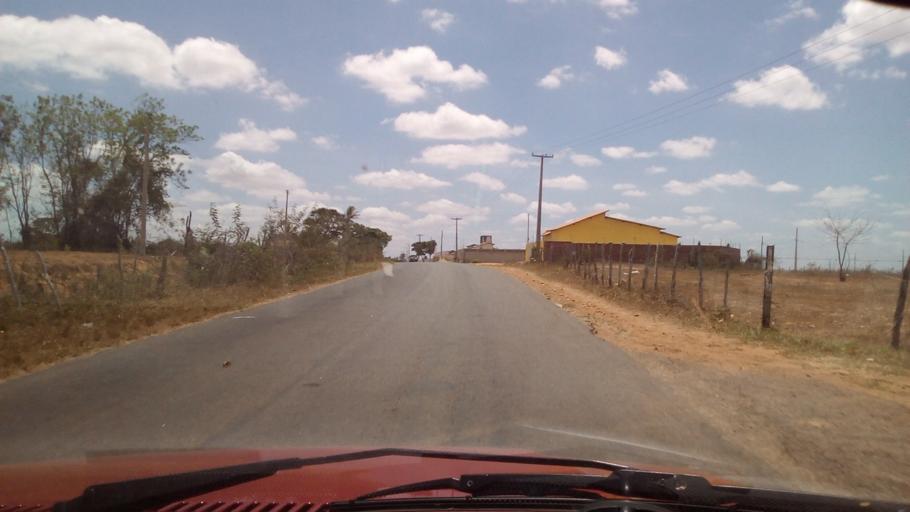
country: BR
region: Paraiba
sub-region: Cacimba De Dentro
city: Cacimba de Dentro
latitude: -6.6218
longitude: -35.7994
